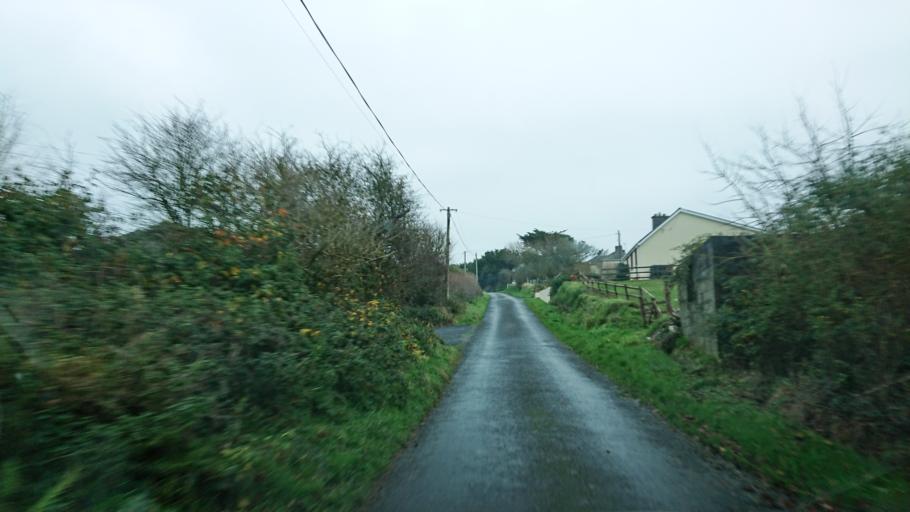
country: IE
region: Munster
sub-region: Waterford
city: Dunmore East
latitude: 52.1452
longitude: -7.0537
